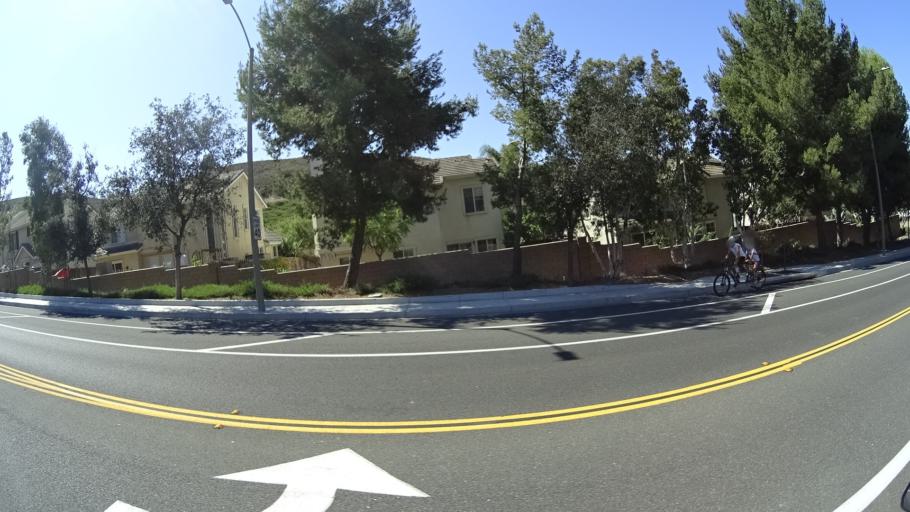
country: US
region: California
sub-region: Orange County
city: San Clemente
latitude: 33.4732
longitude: -117.6151
